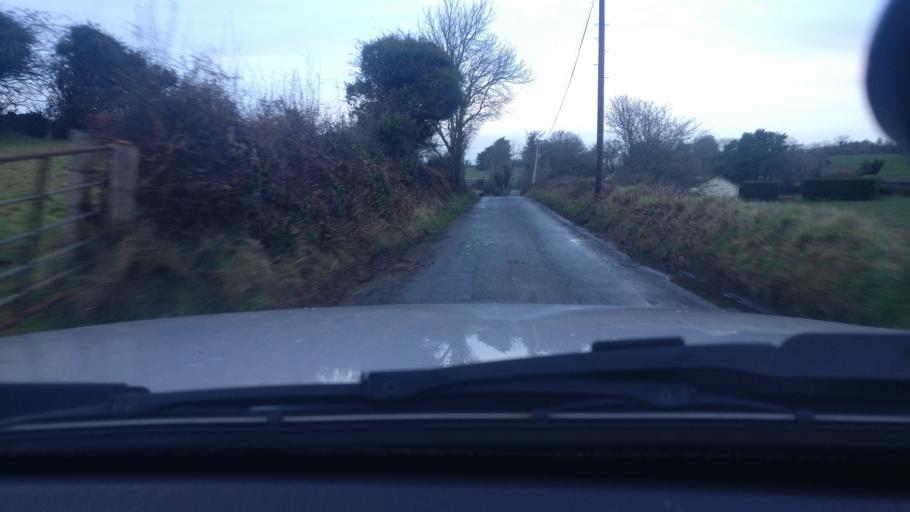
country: IE
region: Connaught
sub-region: County Galway
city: Loughrea
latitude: 53.1690
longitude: -8.5833
